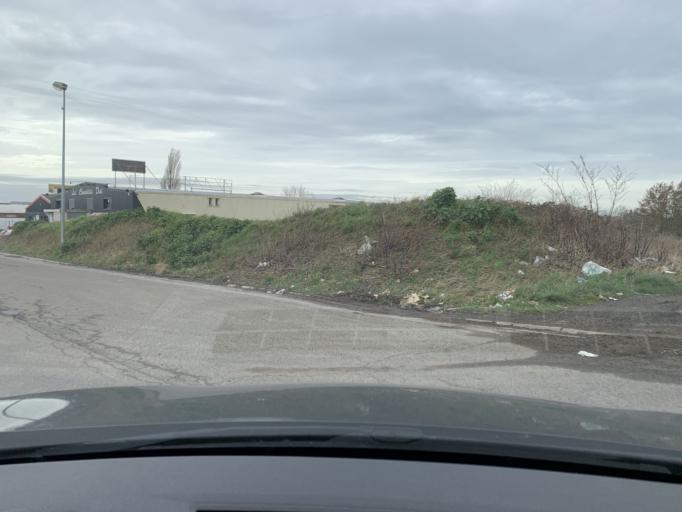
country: FR
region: Nord-Pas-de-Calais
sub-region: Departement du Nord
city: Cambrai
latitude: 50.1486
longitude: 3.2246
